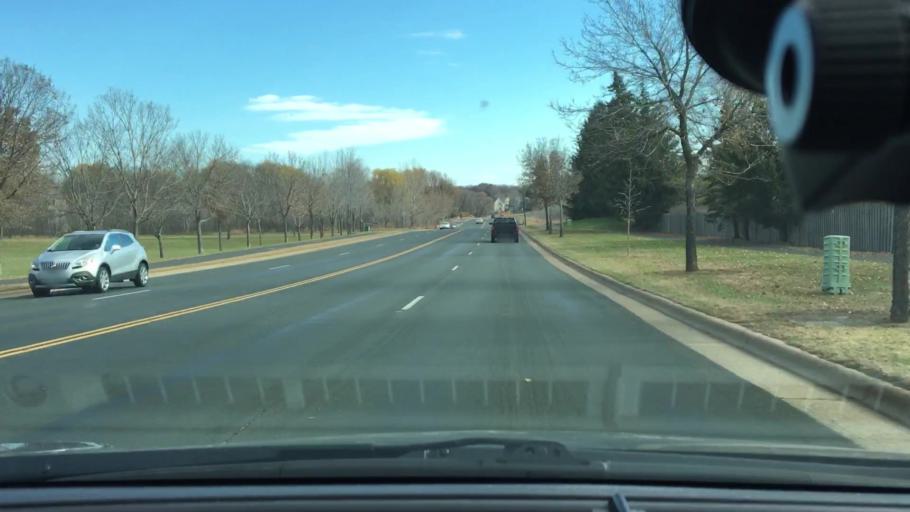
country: US
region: Minnesota
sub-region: Hennepin County
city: Maple Grove
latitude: 45.1085
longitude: -93.4845
